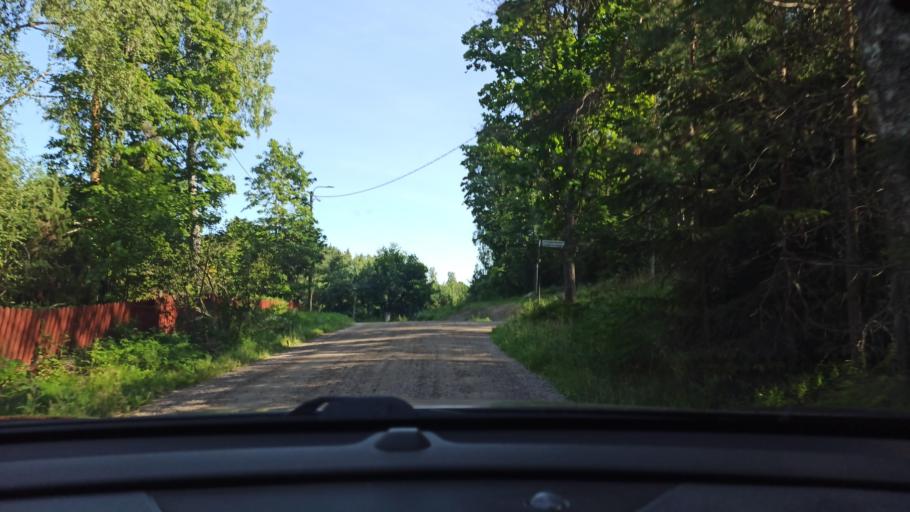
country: FI
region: Uusimaa
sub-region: Helsinki
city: Espoo
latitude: 60.2110
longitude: 24.5508
